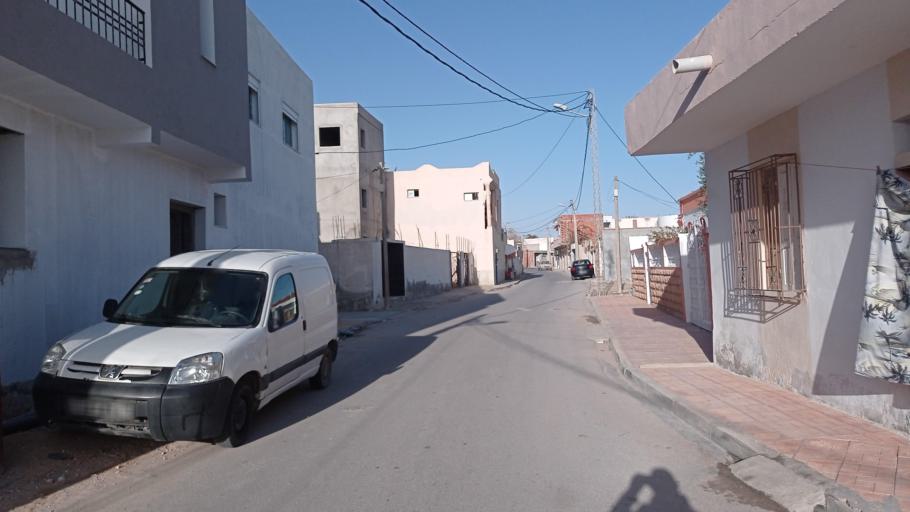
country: TN
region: Qabis
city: Gabes
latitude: 33.8549
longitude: 10.1206
